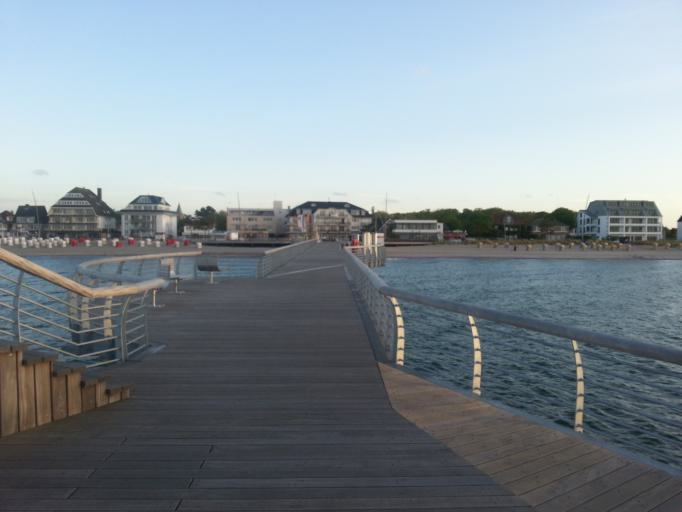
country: DE
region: Schleswig-Holstein
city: Travemuende
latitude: 53.9937
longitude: 10.8324
